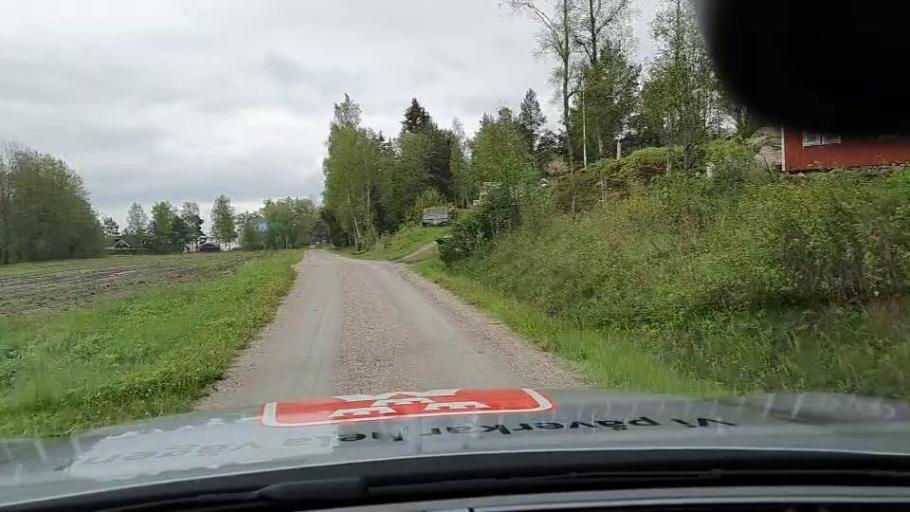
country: SE
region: Soedermanland
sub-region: Nykopings Kommun
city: Svalsta
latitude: 58.6213
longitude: 16.9380
